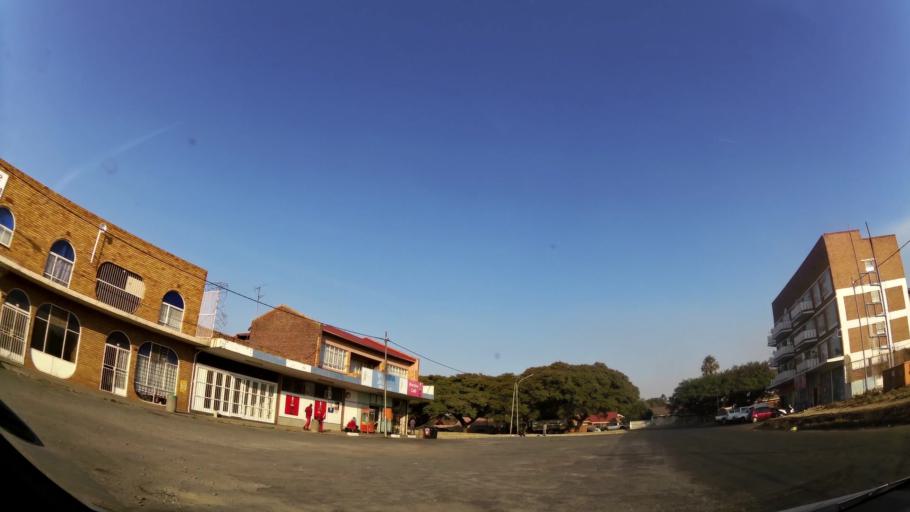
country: ZA
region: Gauteng
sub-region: Ekurhuleni Metropolitan Municipality
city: Springs
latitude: -26.2563
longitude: 28.3920
